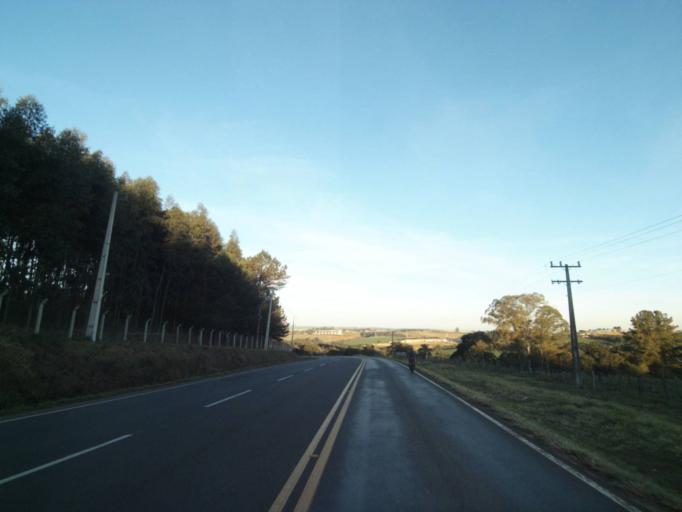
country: BR
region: Parana
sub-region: Tibagi
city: Tibagi
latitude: -24.5125
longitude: -50.4316
